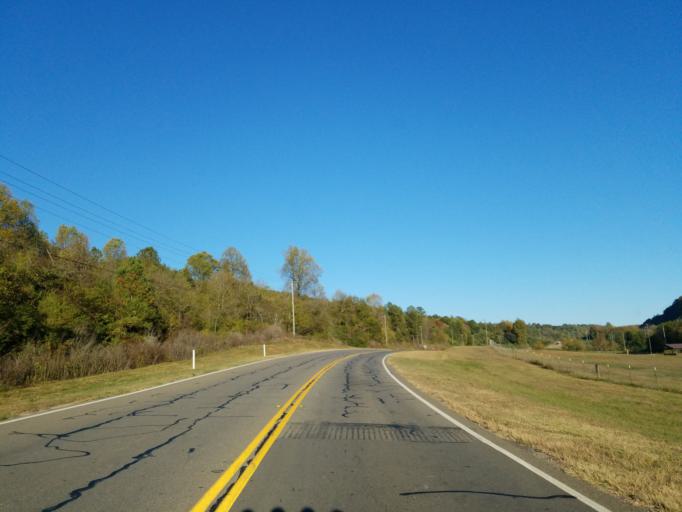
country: US
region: Georgia
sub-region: Pickens County
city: Nelson
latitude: 34.4349
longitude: -84.3593
